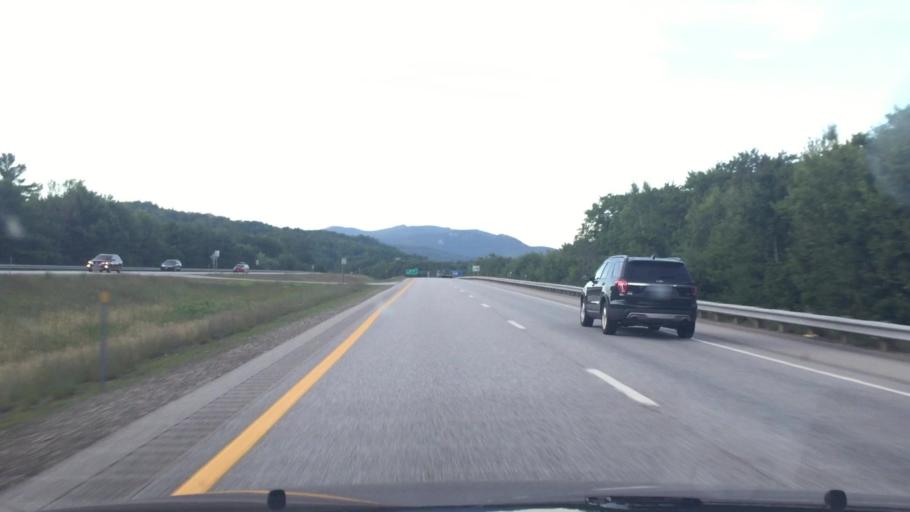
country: US
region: New Hampshire
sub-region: Grafton County
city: Thornton
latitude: 43.8409
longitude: -71.6492
